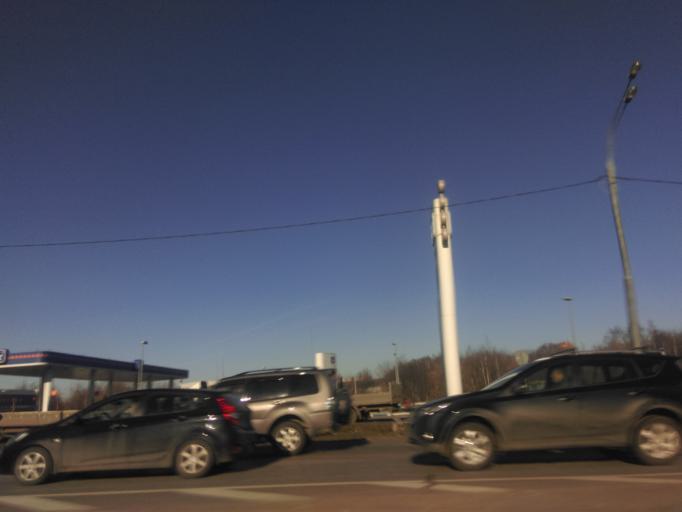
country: RU
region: Moscow
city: Novo-Peredelkino
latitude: 55.6714
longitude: 37.3132
